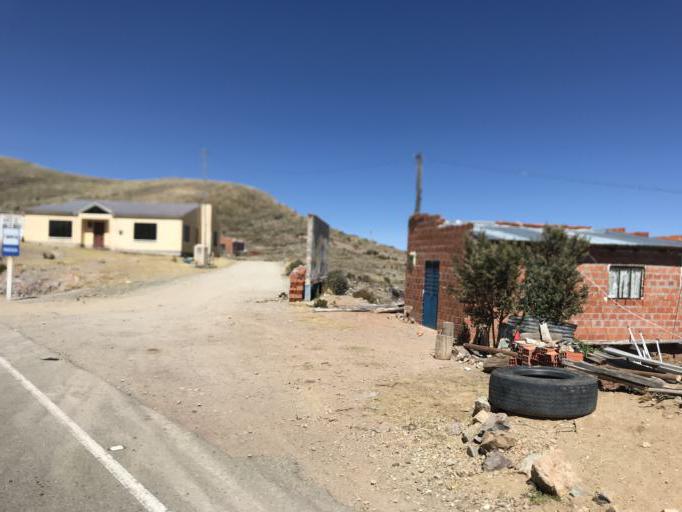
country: BO
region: La Paz
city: San Pedro
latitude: -16.2009
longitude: -68.9029
